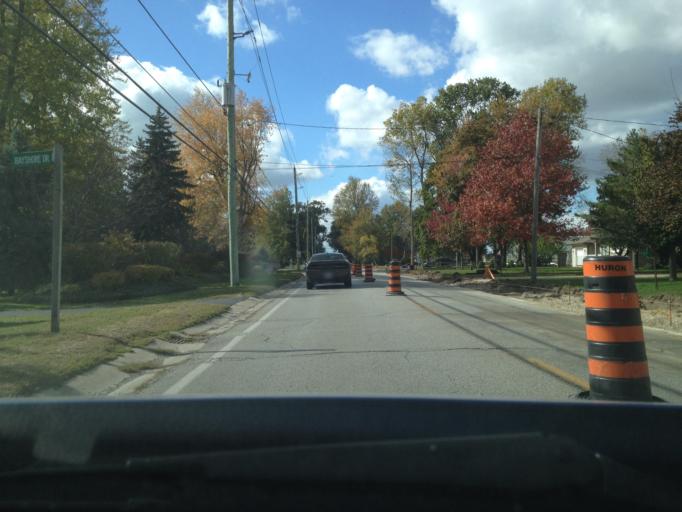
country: CA
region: Ontario
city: Amherstburg
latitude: 42.0344
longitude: -82.6135
